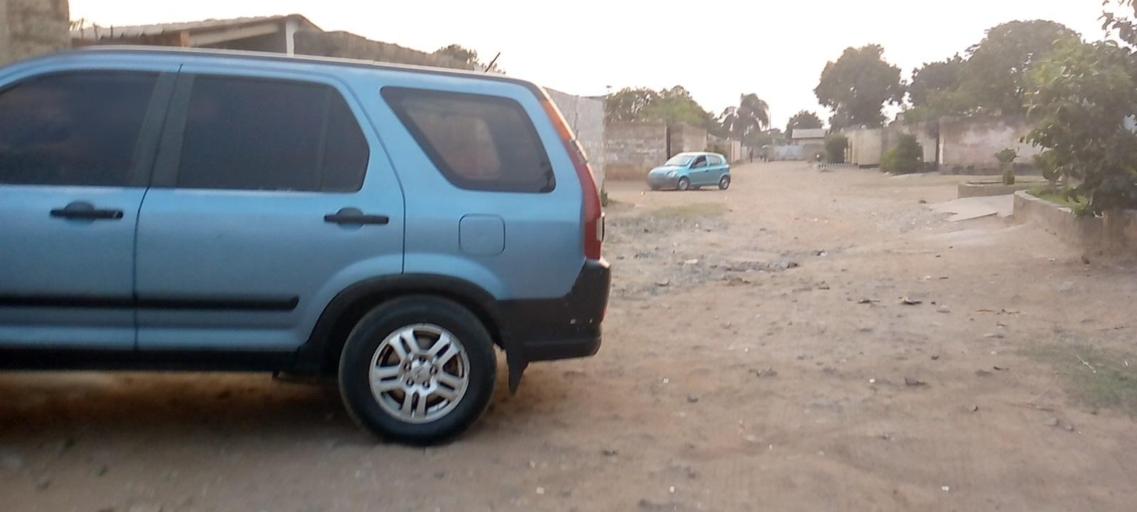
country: ZM
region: Lusaka
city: Lusaka
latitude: -15.4055
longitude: 28.3480
